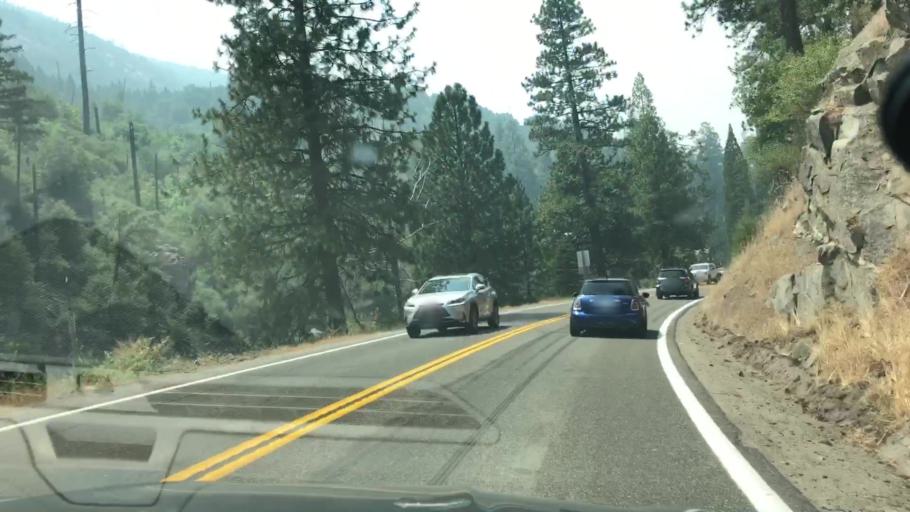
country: US
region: California
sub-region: El Dorado County
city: Pollock Pines
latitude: 38.7737
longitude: -120.3981
